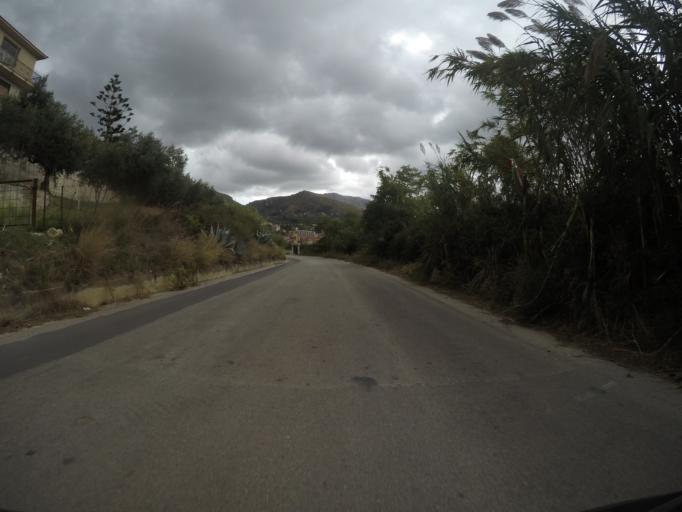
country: IT
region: Sicily
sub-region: Palermo
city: Montelepre
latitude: 38.0941
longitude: 13.1726
